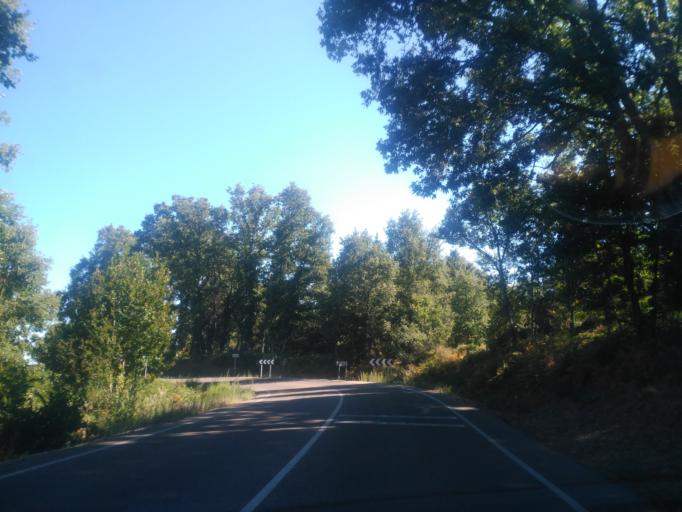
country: ES
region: Castille and Leon
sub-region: Provincia de Zamora
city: Galende
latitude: 42.1003
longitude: -6.6521
